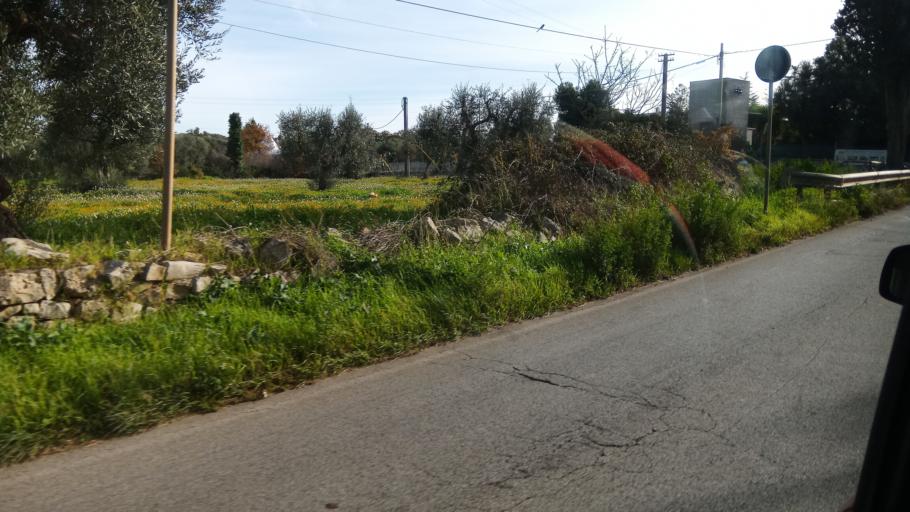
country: IT
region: Apulia
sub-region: Provincia di Bari
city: Castellana
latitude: 40.9017
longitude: 17.1663
